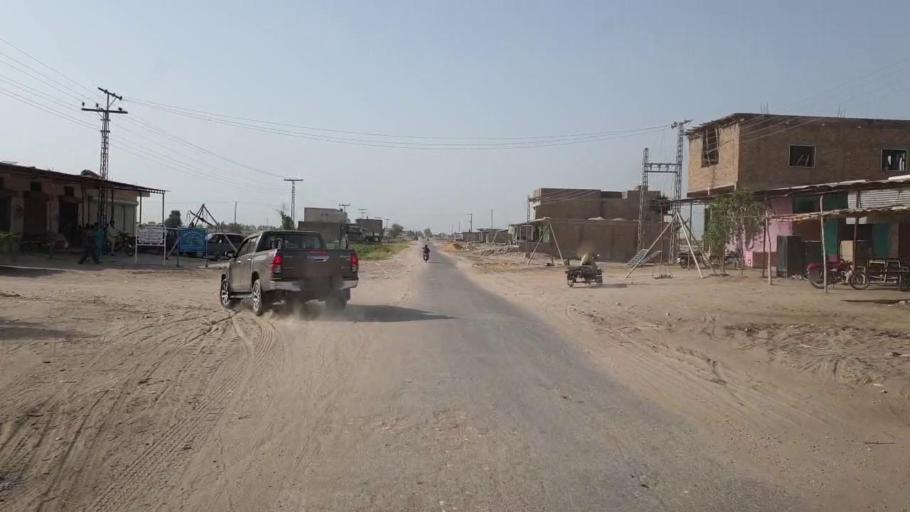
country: PK
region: Sindh
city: Sanghar
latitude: 26.2787
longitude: 68.9303
